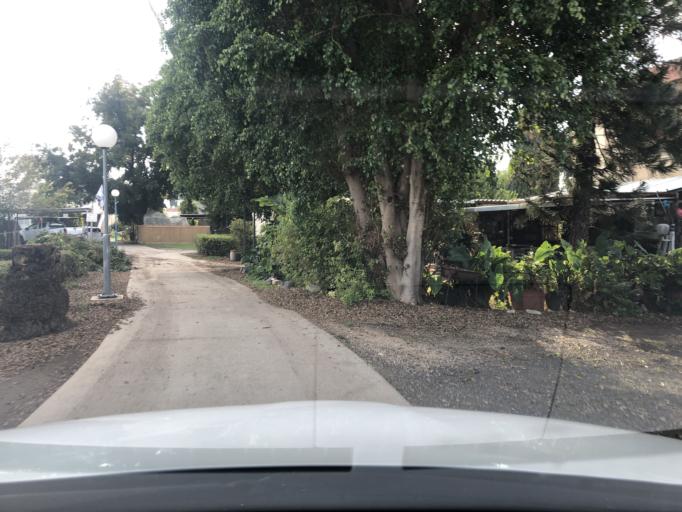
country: IL
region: Northern District
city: Yavne'el
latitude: 32.6617
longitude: 35.5817
